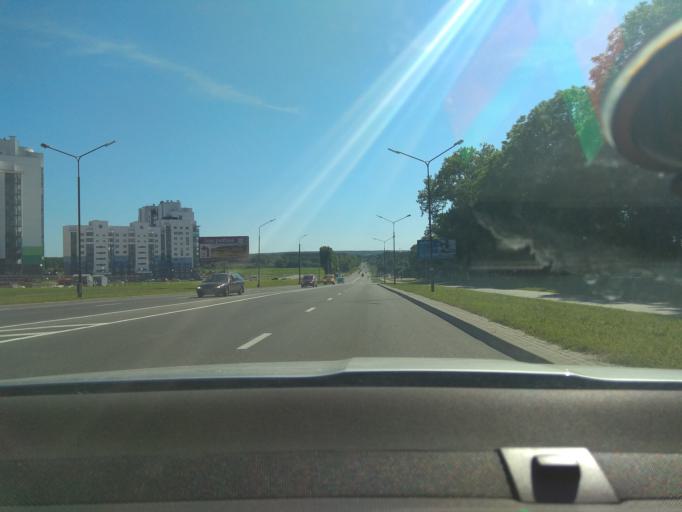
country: BY
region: Grodnenskaya
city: Hrodna
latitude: 53.6485
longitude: 23.7806
